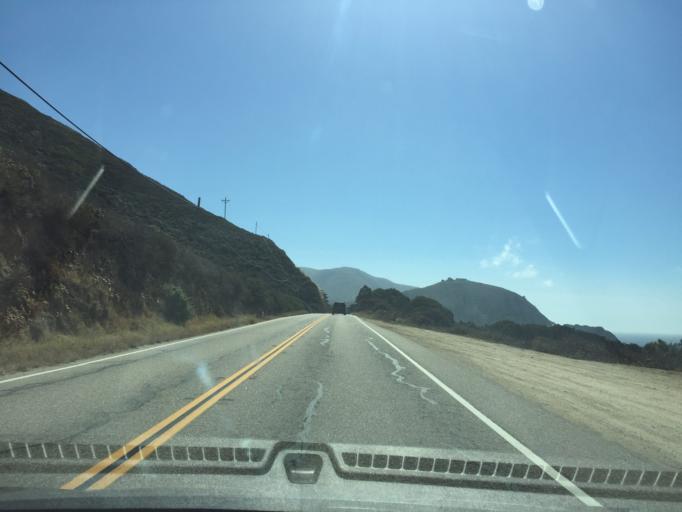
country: US
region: California
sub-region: Monterey County
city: Carmel-by-the-Sea
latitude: 36.3914
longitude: -121.9019
